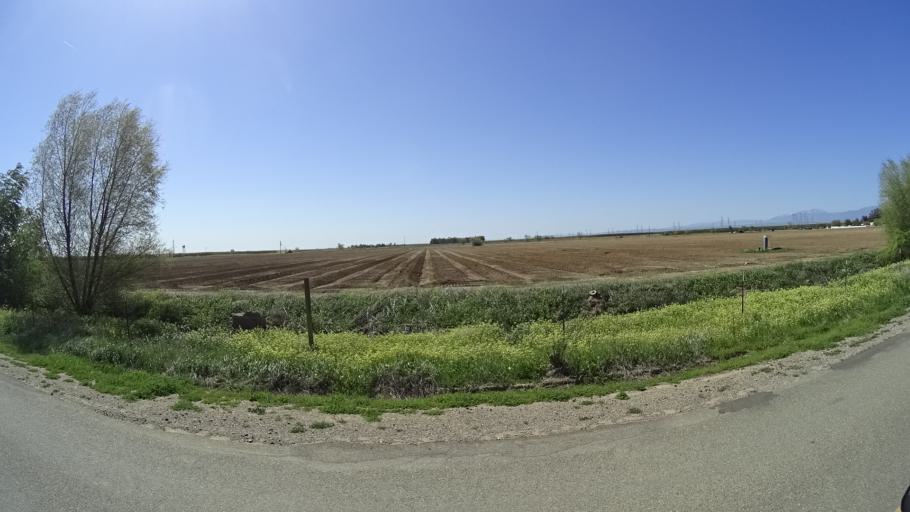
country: US
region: California
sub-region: Glenn County
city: Orland
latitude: 39.6973
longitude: -122.2565
